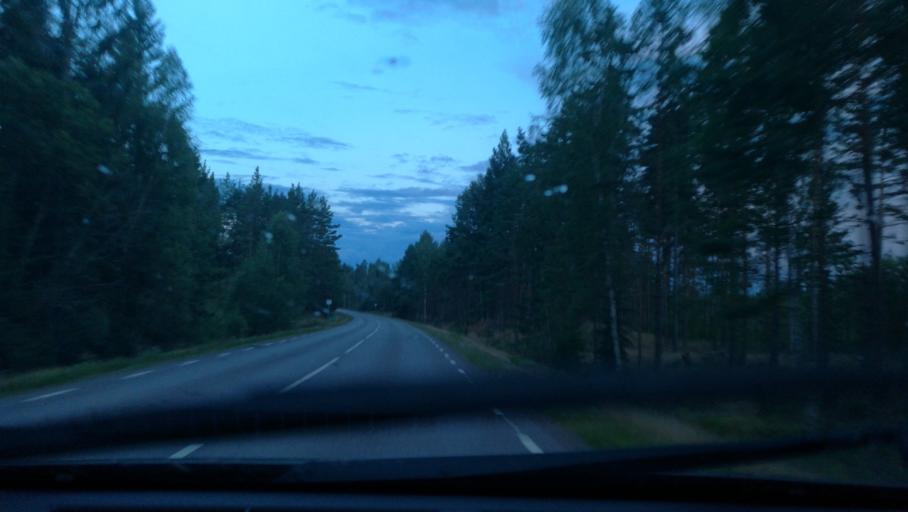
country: SE
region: OEstergoetland
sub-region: Norrkopings Kommun
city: Svartinge
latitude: 58.8099
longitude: 15.9403
